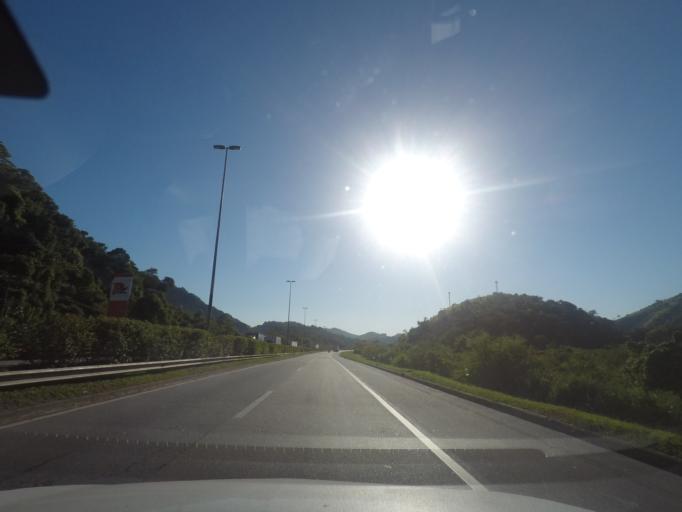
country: BR
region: Rio de Janeiro
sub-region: Petropolis
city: Petropolis
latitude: -22.6537
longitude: -43.1478
